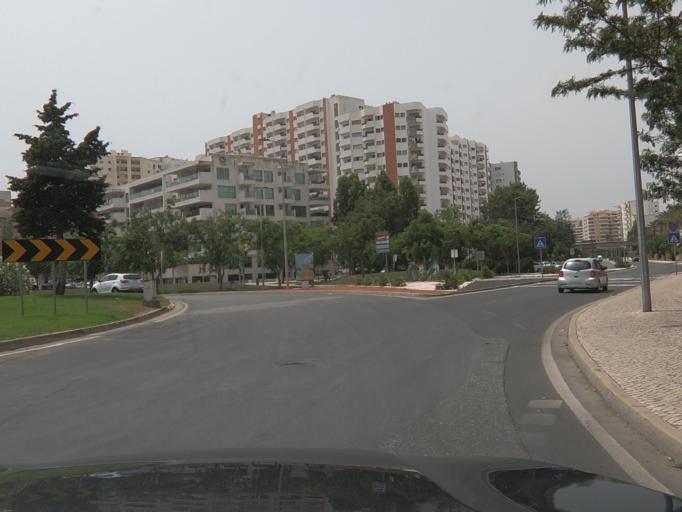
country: PT
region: Faro
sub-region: Portimao
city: Portimao
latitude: 37.1221
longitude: -8.5355
